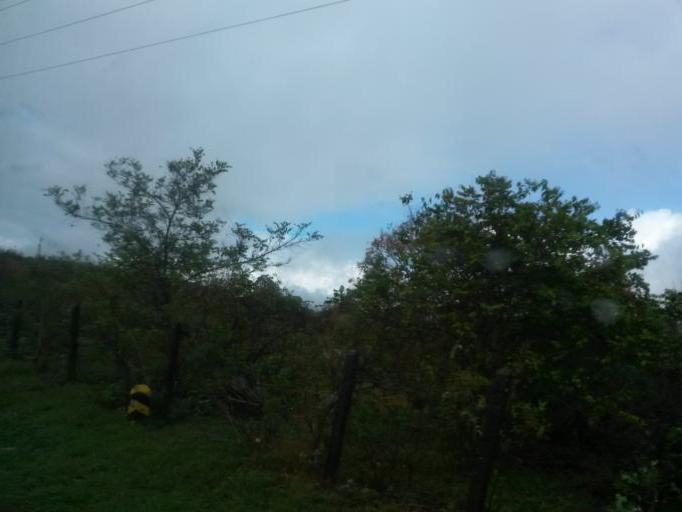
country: CO
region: Cauca
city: El Bordo
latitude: 2.1492
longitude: -76.9211
